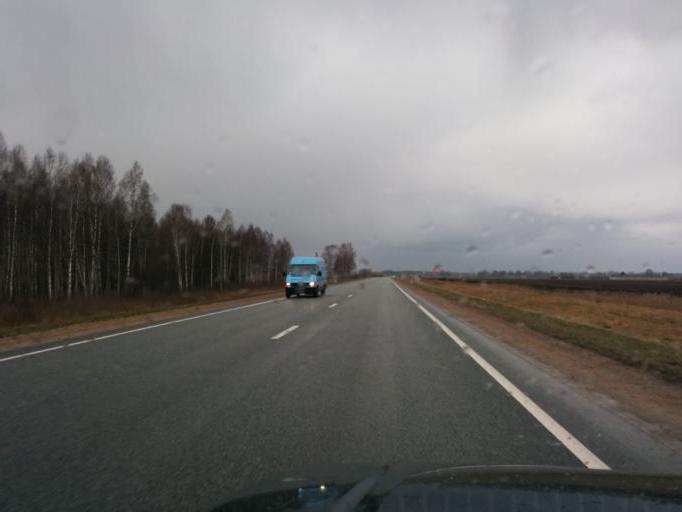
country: LV
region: Marupe
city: Marupe
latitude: 56.8611
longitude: 23.9855
